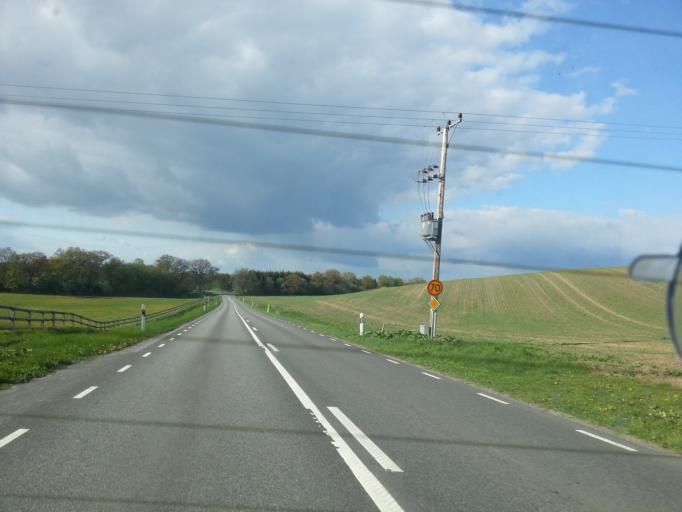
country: SE
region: Skane
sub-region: Sjobo Kommun
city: Sjoebo
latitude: 55.5541
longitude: 13.7463
